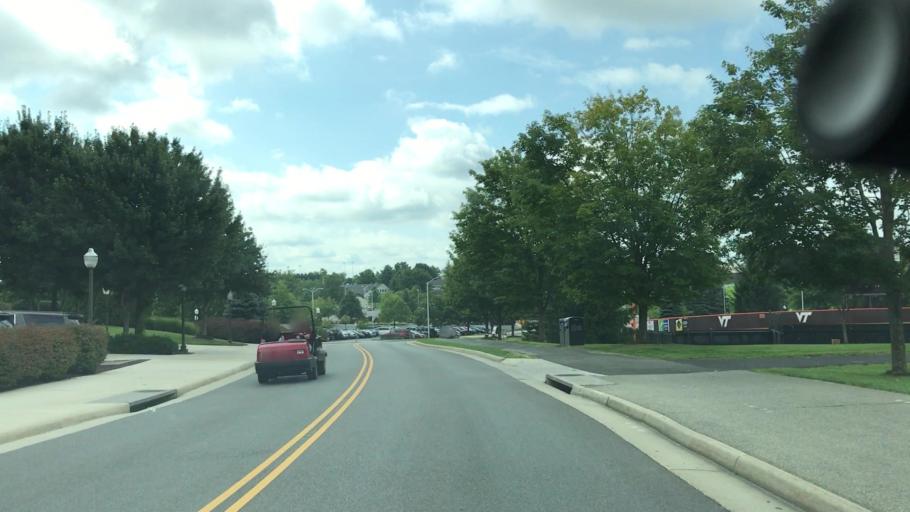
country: US
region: Virginia
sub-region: Montgomery County
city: Blacksburg
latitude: 37.2196
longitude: -80.4196
